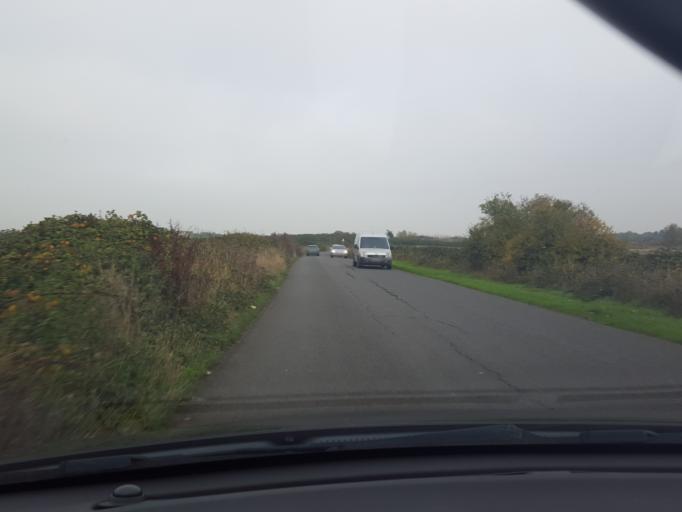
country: GB
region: England
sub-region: Essex
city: Saint Osyth
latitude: 51.7799
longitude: 1.0883
